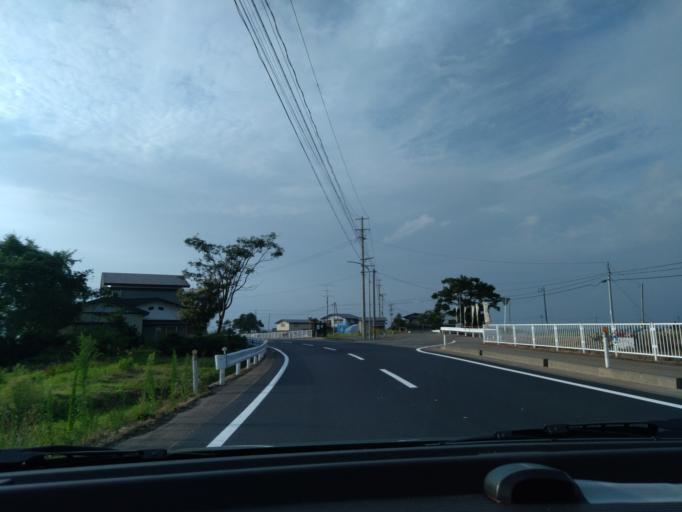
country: JP
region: Akita
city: Yokotemachi
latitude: 39.3774
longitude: 140.5339
